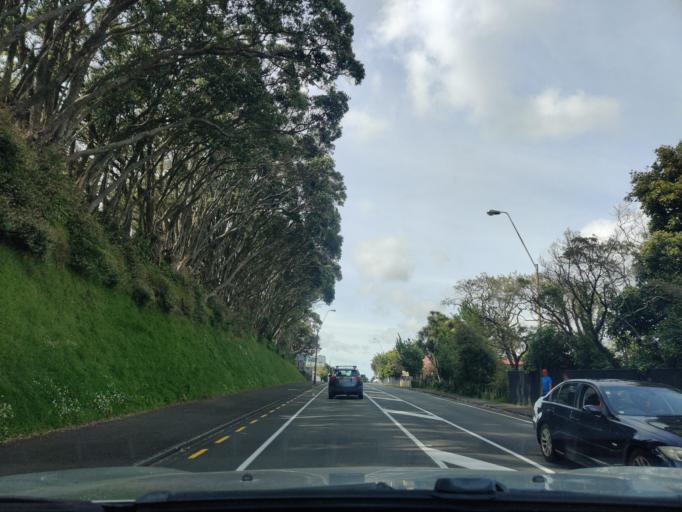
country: NZ
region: Taranaki
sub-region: New Plymouth District
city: New Plymouth
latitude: -39.0596
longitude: 174.0850
